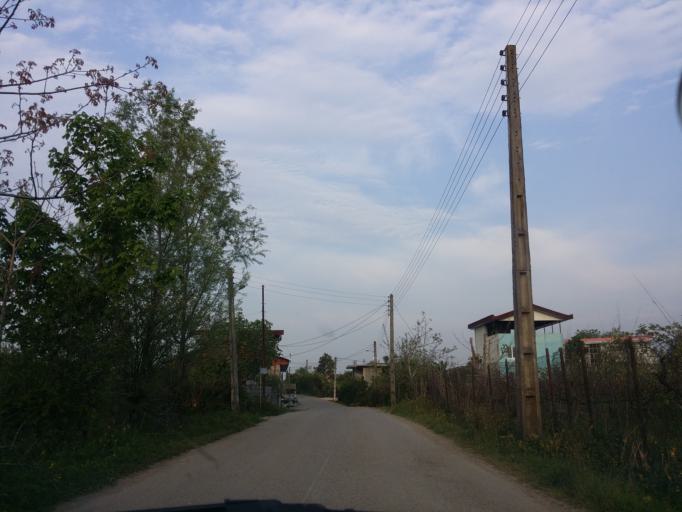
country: IR
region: Mazandaran
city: Chalus
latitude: 36.6657
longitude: 51.3699
